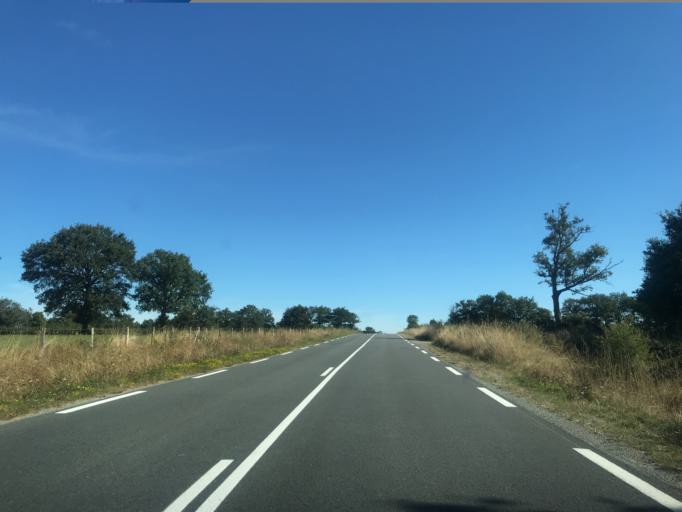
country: FR
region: Limousin
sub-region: Departement de la Creuse
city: Gouzon
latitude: 46.1562
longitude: 2.2099
